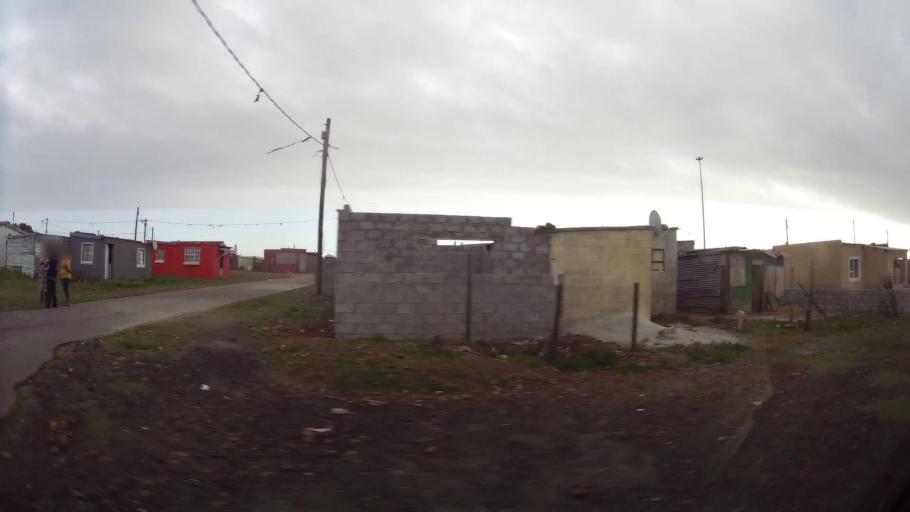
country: ZA
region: Eastern Cape
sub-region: Nelson Mandela Bay Metropolitan Municipality
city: Port Elizabeth
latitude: -33.9102
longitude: 25.5391
